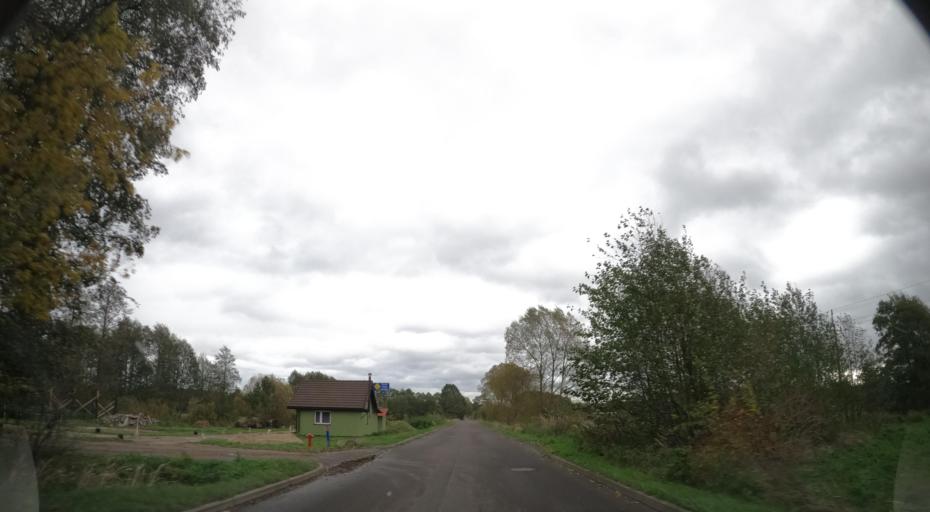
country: PL
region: West Pomeranian Voivodeship
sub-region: Powiat goleniowski
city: Stepnica
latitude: 53.6499
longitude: 14.6420
